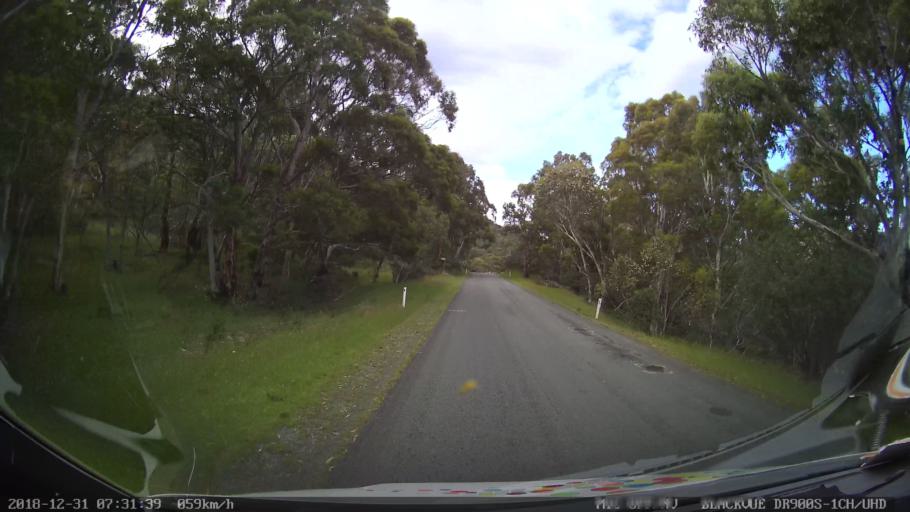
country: AU
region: New South Wales
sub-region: Snowy River
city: Jindabyne
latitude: -36.3268
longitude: 148.4715
